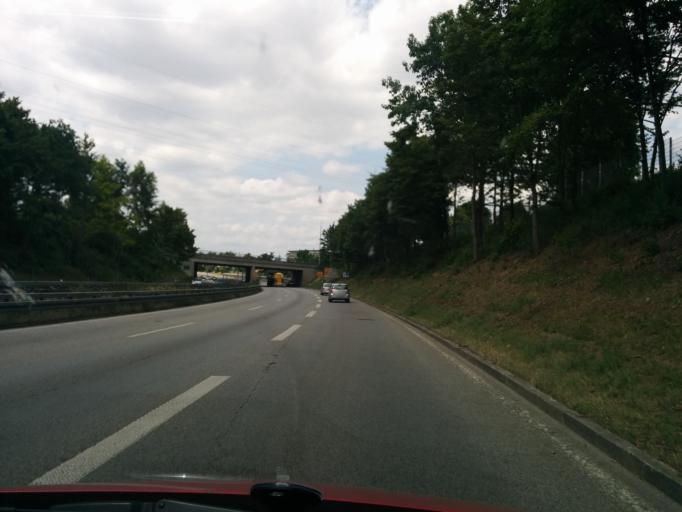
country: DE
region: Bavaria
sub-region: Swabia
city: Augsburg
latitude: 48.3410
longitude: 10.8894
